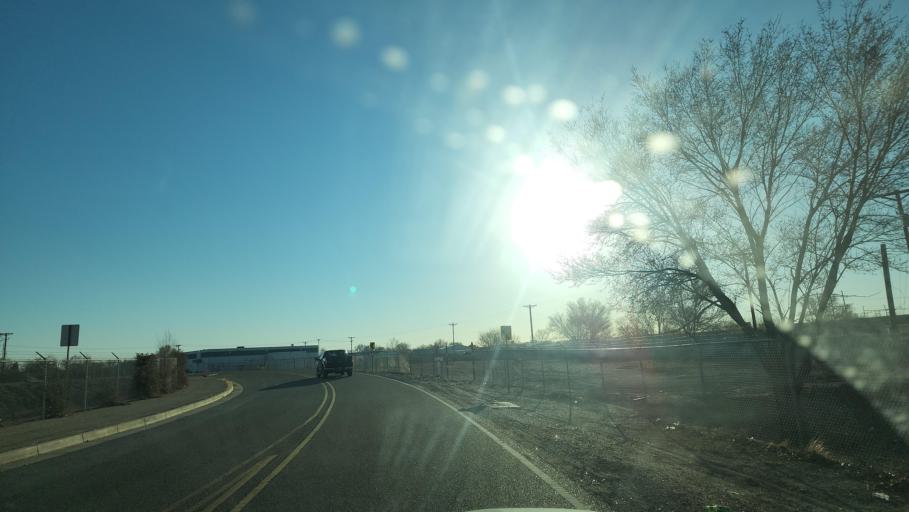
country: US
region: New Mexico
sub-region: Bernalillo County
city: South Valley
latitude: 35.0251
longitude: -106.6537
